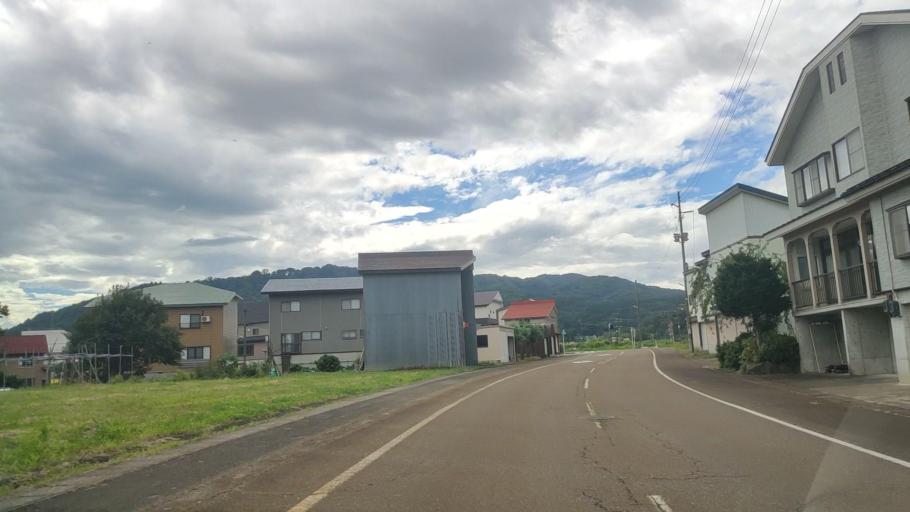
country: JP
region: Niigata
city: Arai
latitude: 37.0075
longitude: 138.2579
